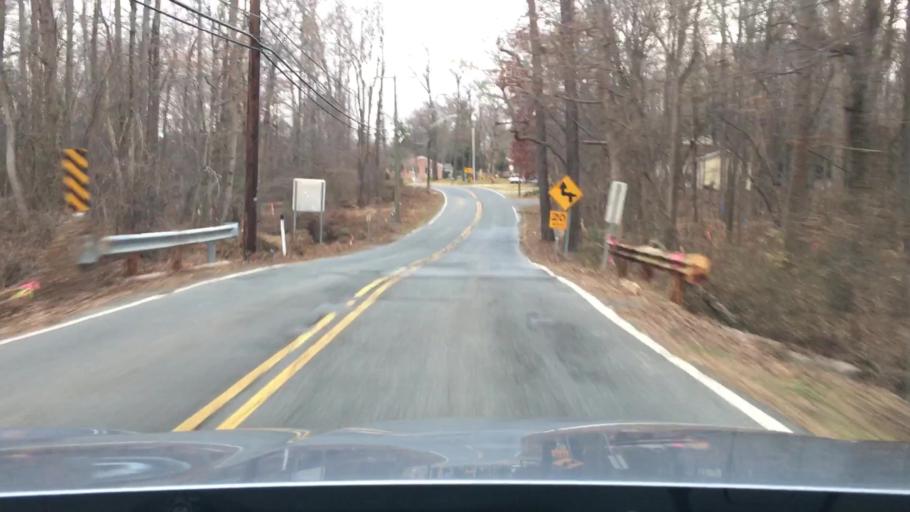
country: US
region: Maryland
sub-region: Prince George's County
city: Glenn Dale
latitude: 38.9953
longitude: -76.7752
